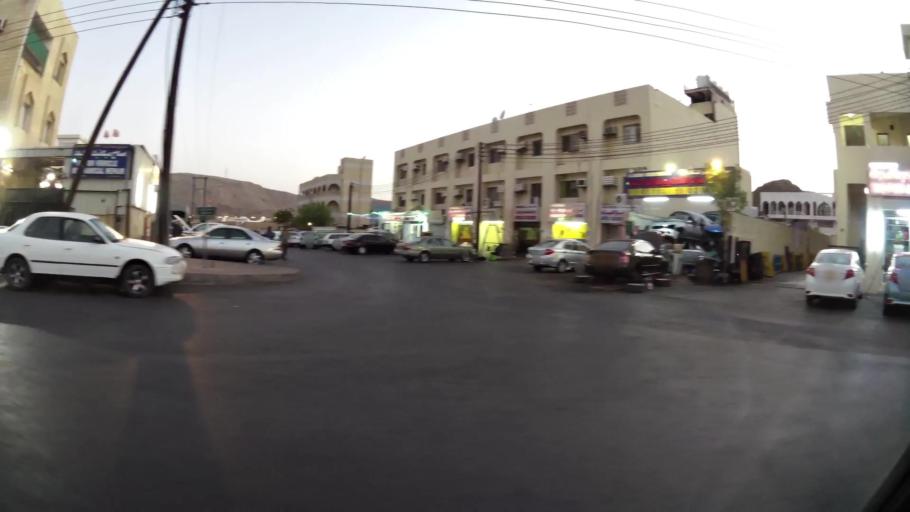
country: OM
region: Muhafazat Masqat
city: Muscat
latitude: 23.5917
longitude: 58.5608
